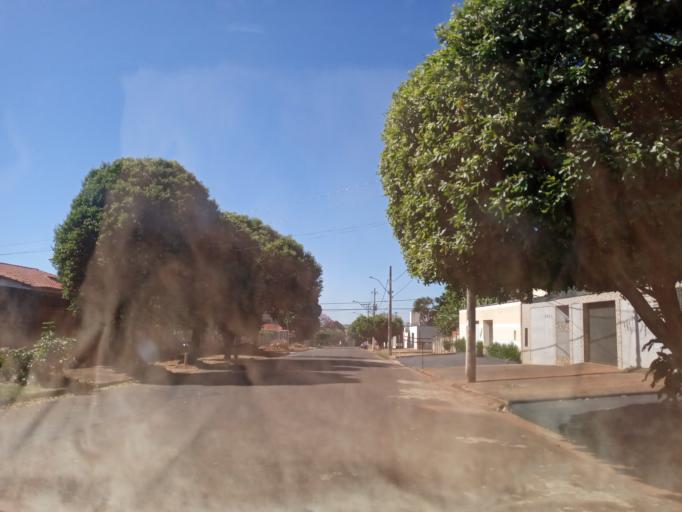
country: BR
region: Minas Gerais
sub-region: Ituiutaba
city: Ituiutaba
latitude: -18.9904
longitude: -49.4514
